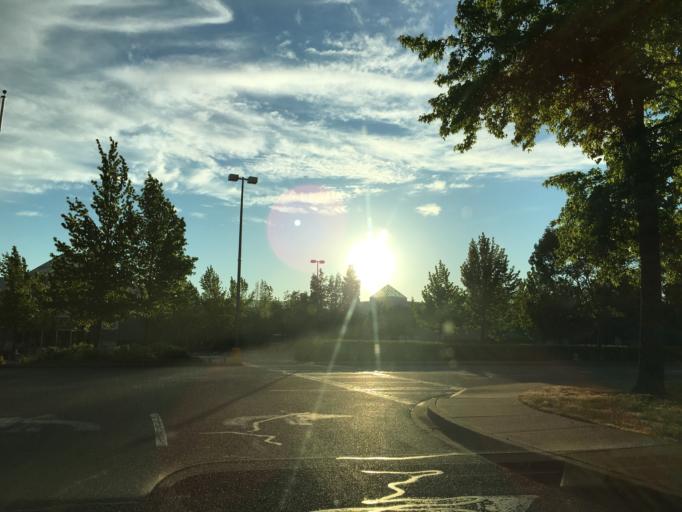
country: US
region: Washington
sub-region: Skagit County
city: Burlington
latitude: 48.4622
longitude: -122.3368
